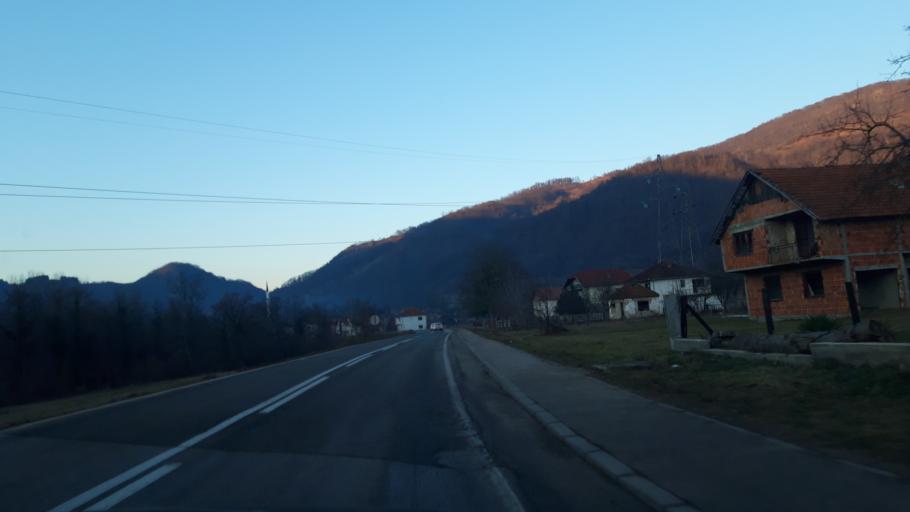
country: BA
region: Republika Srpska
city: Milici
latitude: 44.2471
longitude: 19.1107
